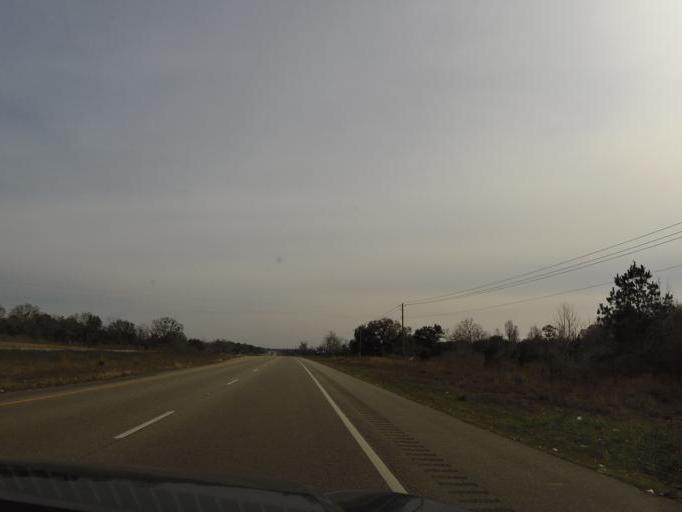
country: US
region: Alabama
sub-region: Houston County
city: Ashford
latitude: 31.1562
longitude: -85.1828
